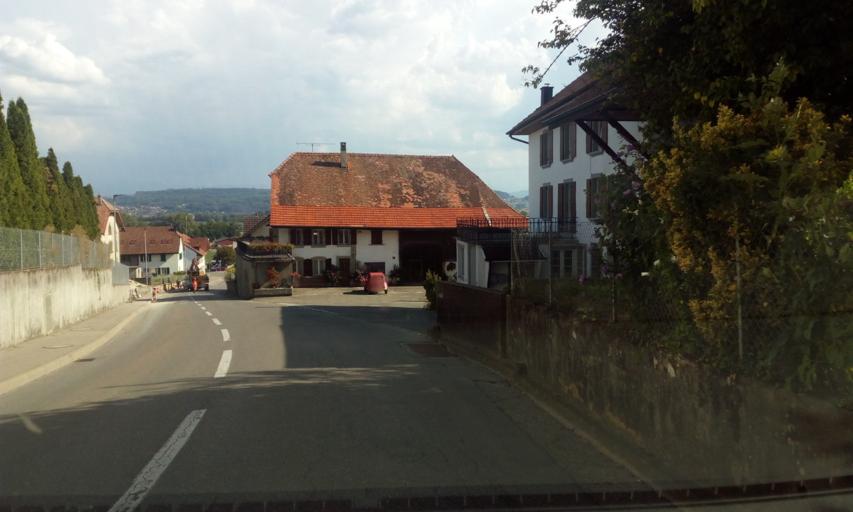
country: CH
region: Fribourg
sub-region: Broye District
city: Domdidier
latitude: 46.8891
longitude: 6.9812
